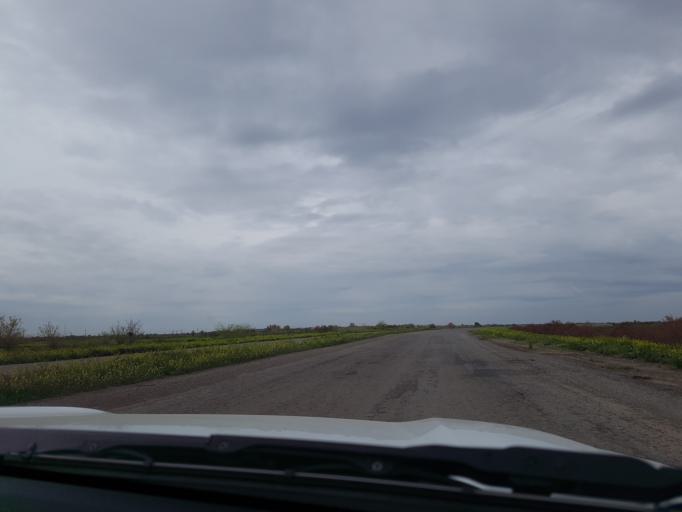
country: TM
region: Mary
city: Bayramaly
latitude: 37.7918
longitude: 62.5516
